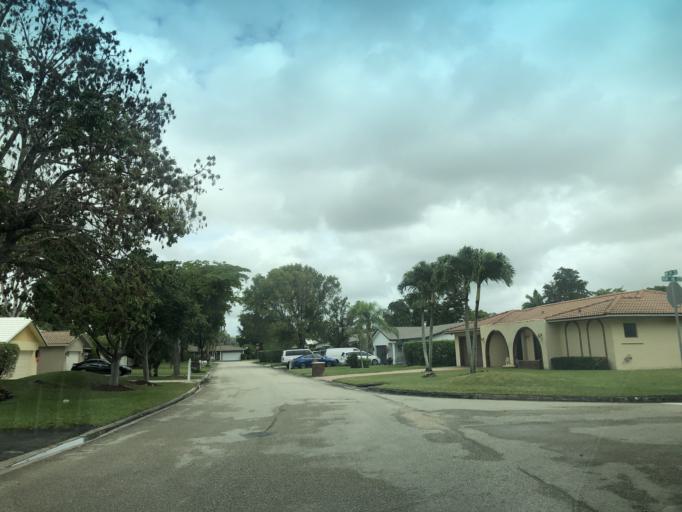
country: US
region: Florida
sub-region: Broward County
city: Coral Springs
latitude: 26.2549
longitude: -80.2433
